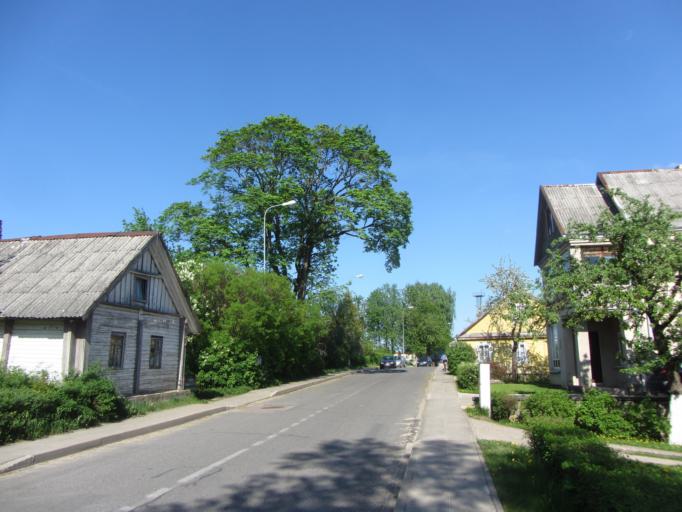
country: LT
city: Moletai
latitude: 55.2311
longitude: 25.4141
